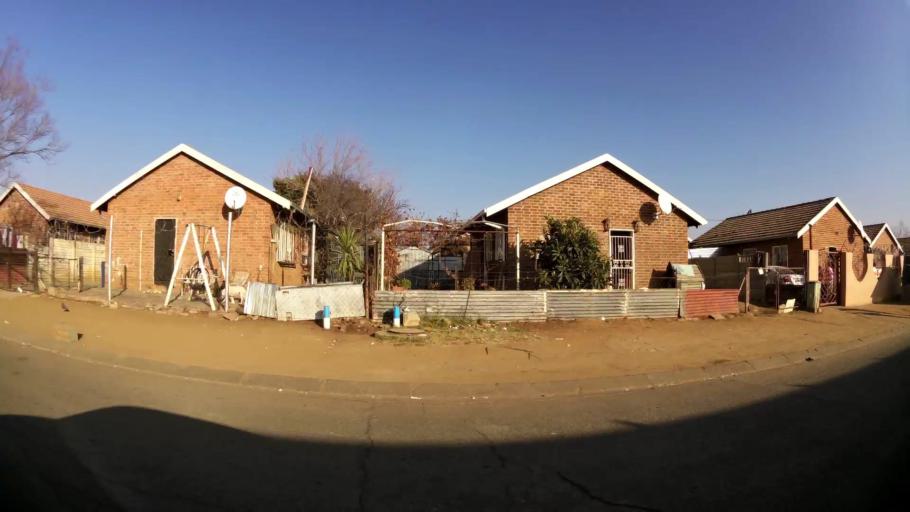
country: ZA
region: Orange Free State
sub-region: Mangaung Metropolitan Municipality
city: Bloemfontein
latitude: -29.1558
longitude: 26.2158
